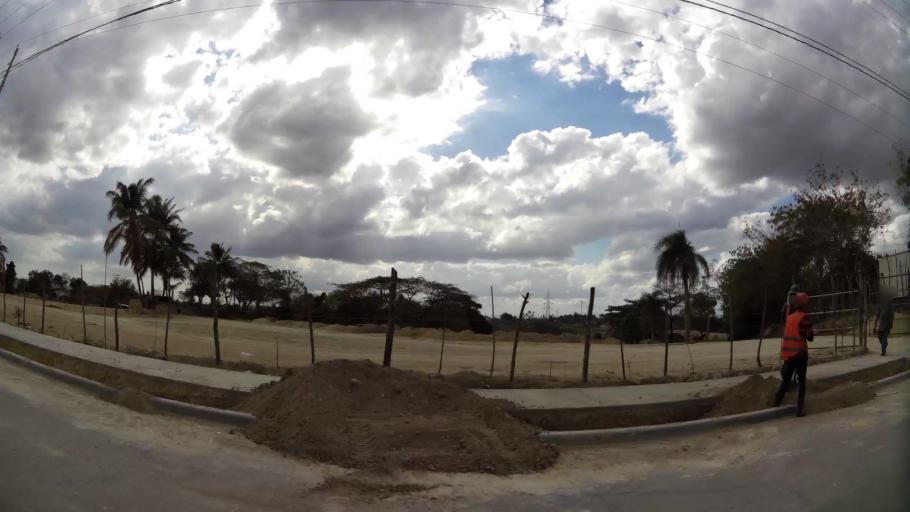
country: DO
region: Nacional
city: Ensanche Luperon
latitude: 18.5328
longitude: -69.8855
